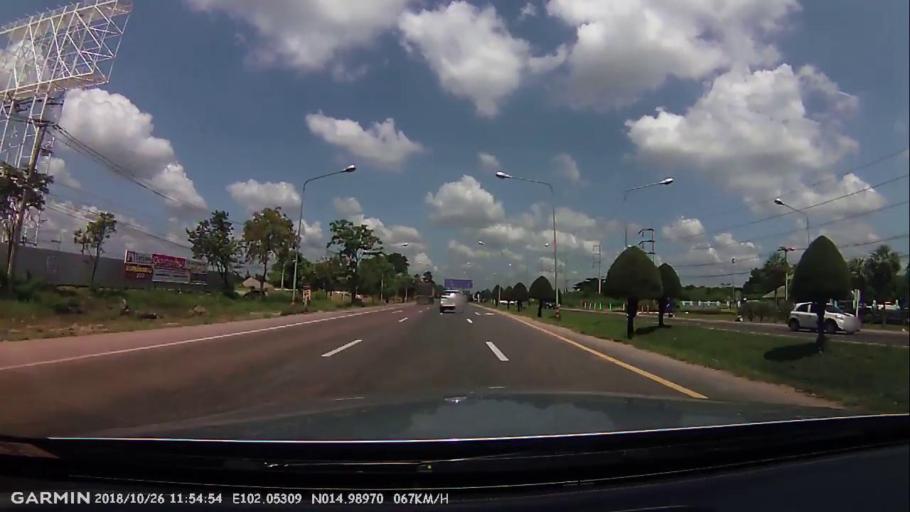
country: TH
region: Nakhon Ratchasima
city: Nakhon Ratchasima
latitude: 14.9899
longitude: 102.0531
